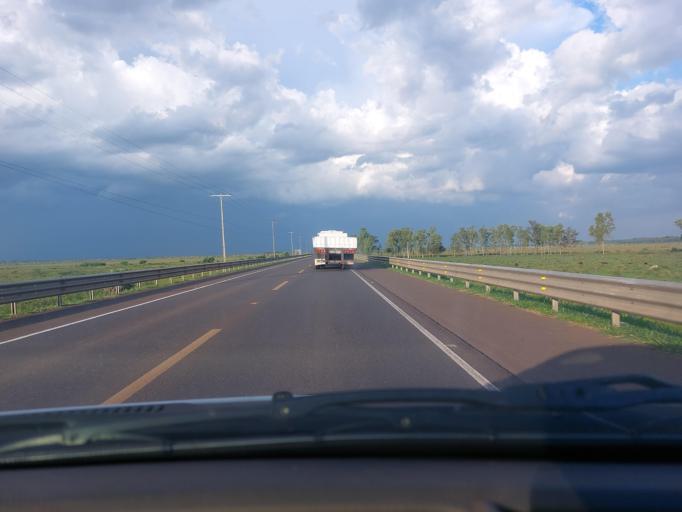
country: PY
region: Cordillera
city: Arroyos y Esteros
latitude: -25.0499
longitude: -57.0818
